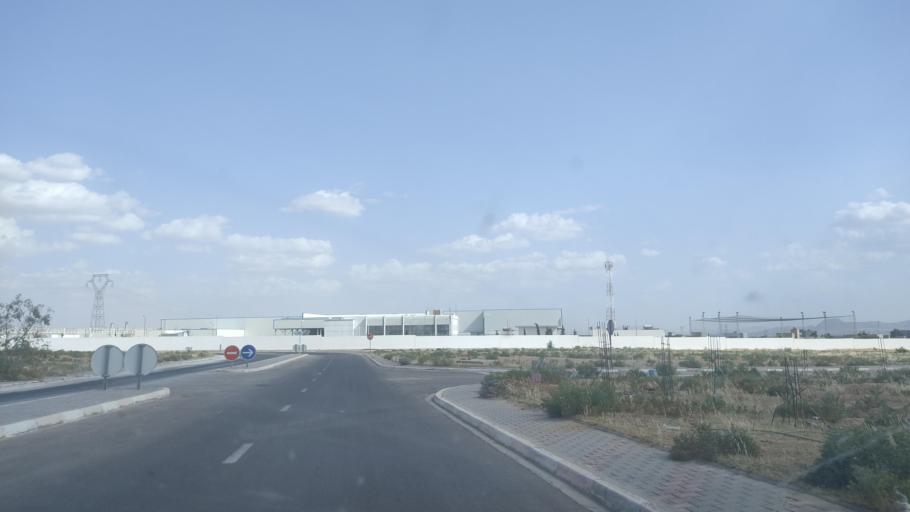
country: TN
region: Sidi Bu Zayd
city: Sidi Bouzid
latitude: 35.1058
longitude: 9.5451
